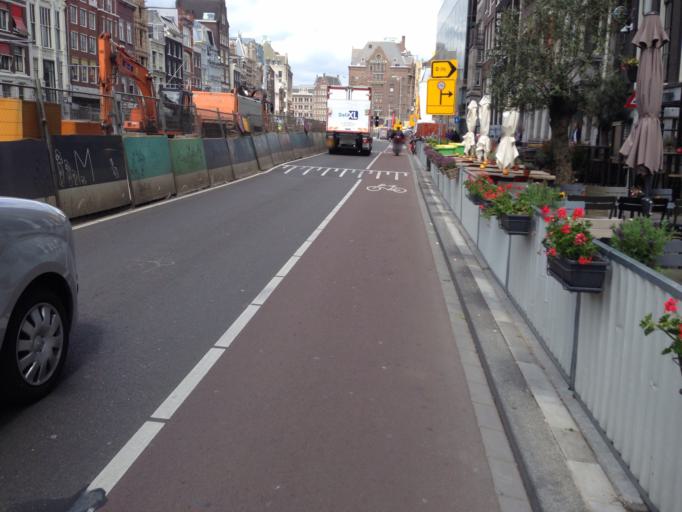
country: NL
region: North Holland
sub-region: Gemeente Amsterdam
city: Amsterdam
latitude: 52.3703
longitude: 4.8927
